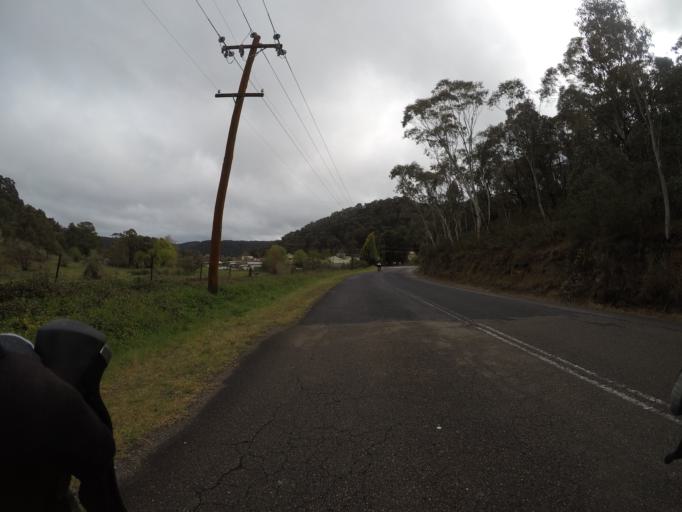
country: AU
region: New South Wales
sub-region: Lithgow
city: Lithgow
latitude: -33.4852
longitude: 150.1759
